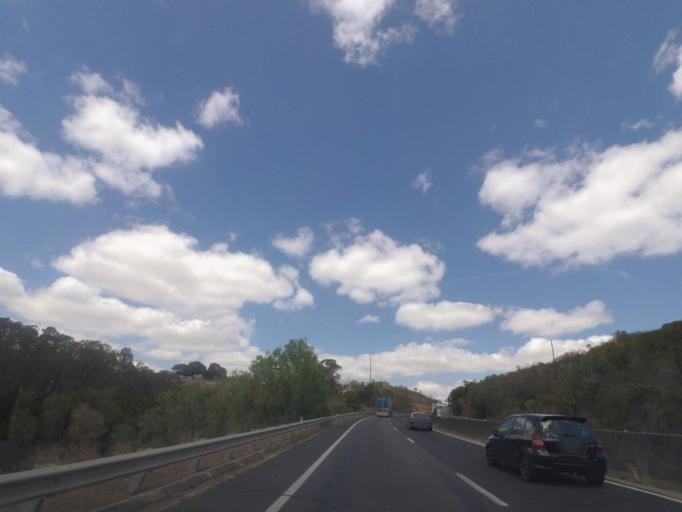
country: AU
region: Queensland
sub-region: Ipswich
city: Thagoona
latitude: -27.5654
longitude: 152.5691
